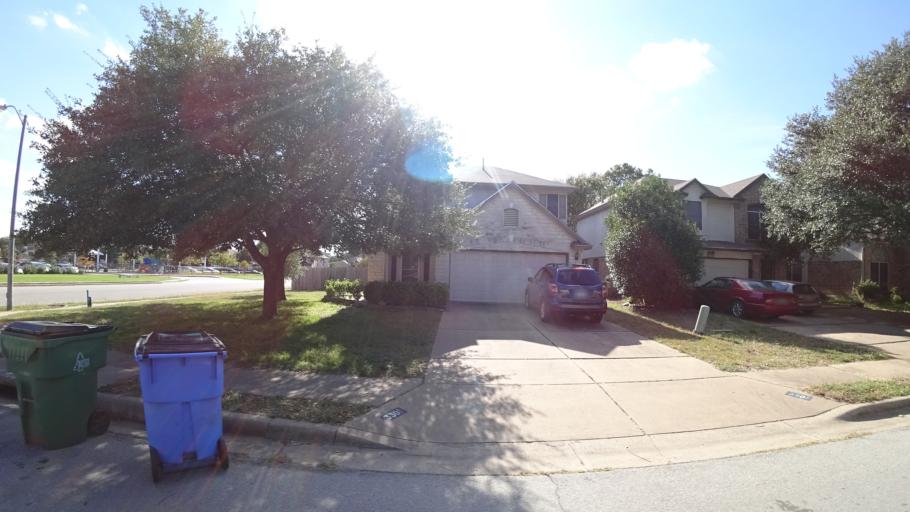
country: US
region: Texas
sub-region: Travis County
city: Wells Branch
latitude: 30.4577
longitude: -97.6833
